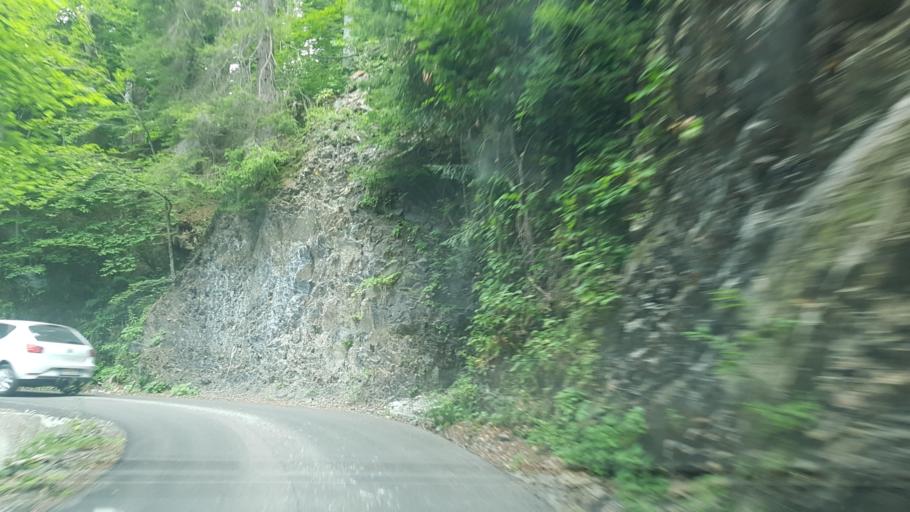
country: IT
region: Friuli Venezia Giulia
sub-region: Provincia di Udine
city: Paularo
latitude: 46.5586
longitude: 13.1260
